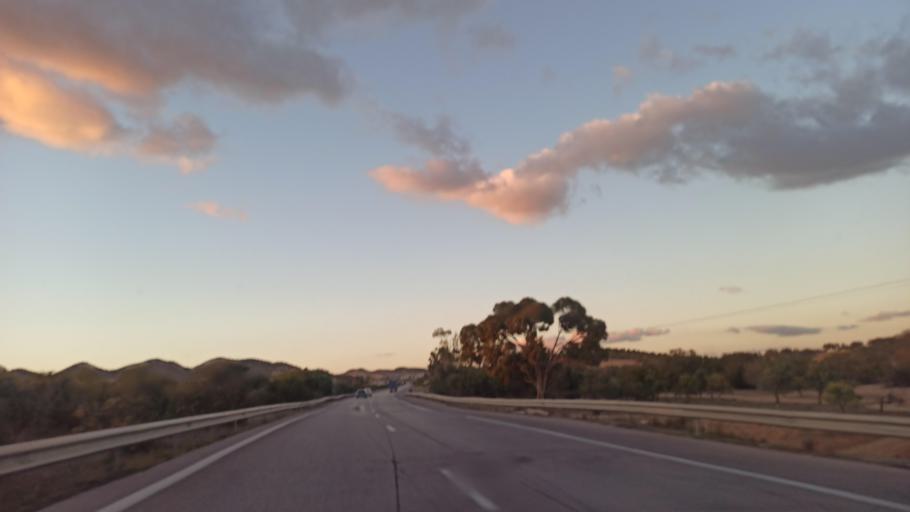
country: TN
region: Susah
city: Harqalah
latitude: 36.2165
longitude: 10.4200
